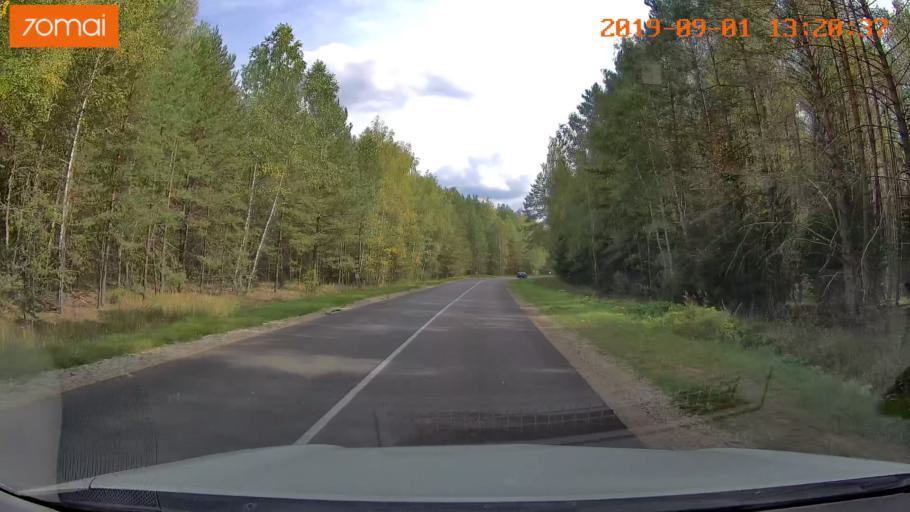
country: RU
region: Kaluga
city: Maloyaroslavets
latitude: 54.9111
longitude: 36.5021
